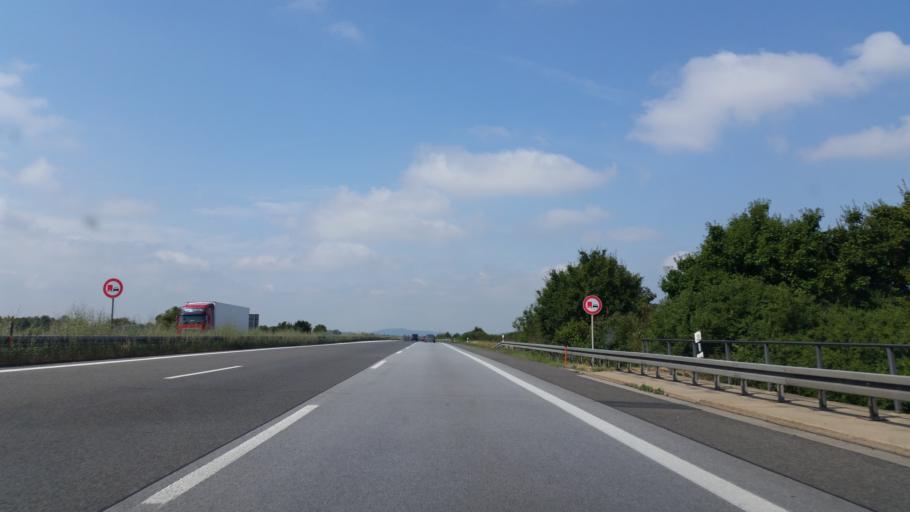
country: DE
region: Saxony
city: Crostwitz
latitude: 51.2028
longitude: 14.2721
